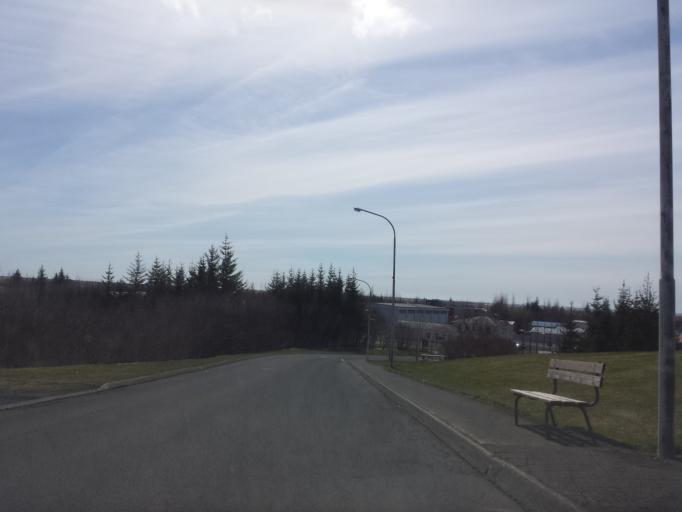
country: IS
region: South
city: Hveragerdi
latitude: 64.0025
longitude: -21.1842
